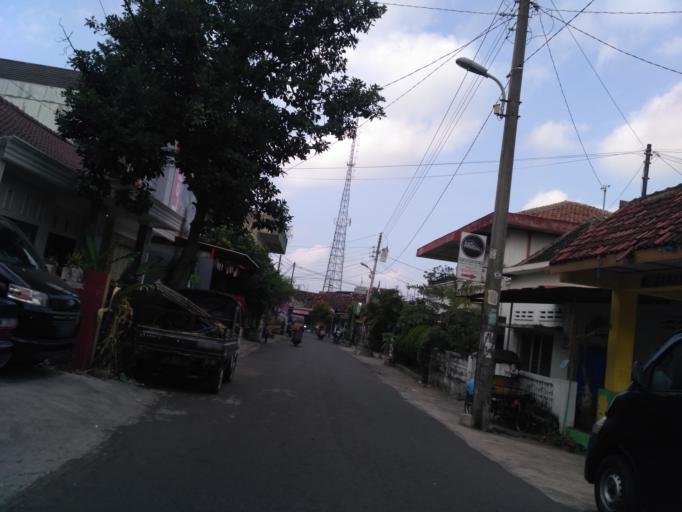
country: ID
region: Daerah Istimewa Yogyakarta
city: Yogyakarta
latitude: -7.7957
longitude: 110.3710
